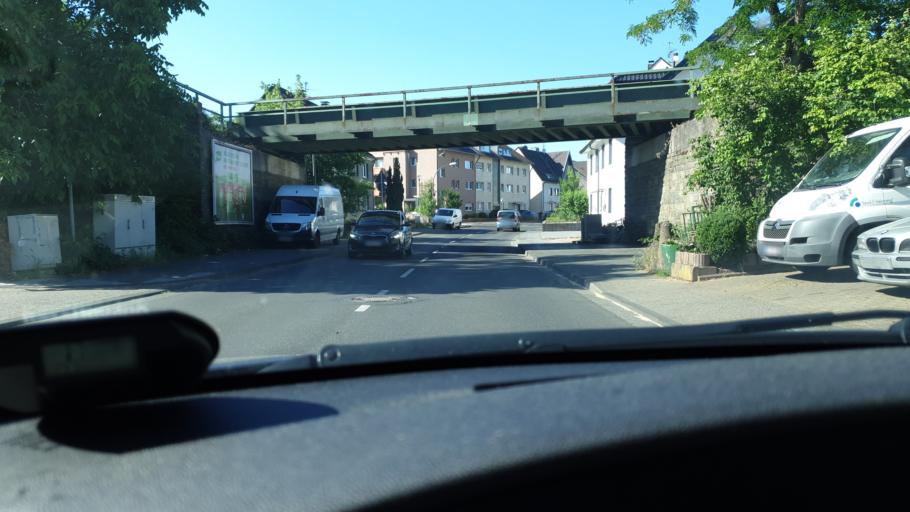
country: DE
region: North Rhine-Westphalia
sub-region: Regierungsbezirk Koln
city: Rath
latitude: 50.9159
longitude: 7.0813
